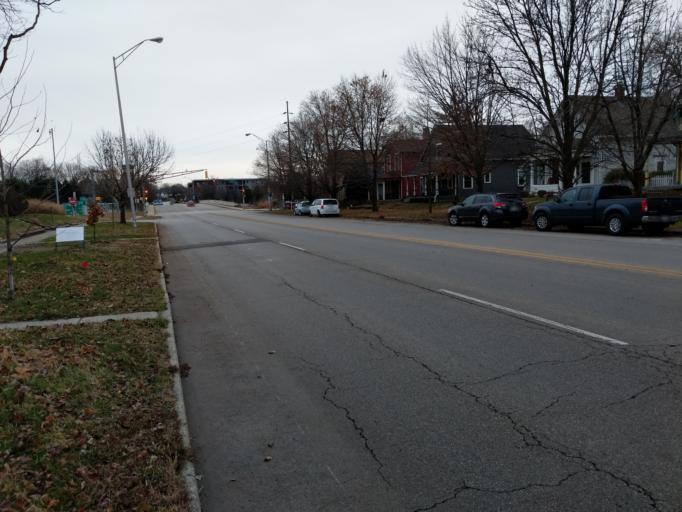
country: US
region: Indiana
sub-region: Marion County
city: Indianapolis
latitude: 39.7607
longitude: -86.1450
